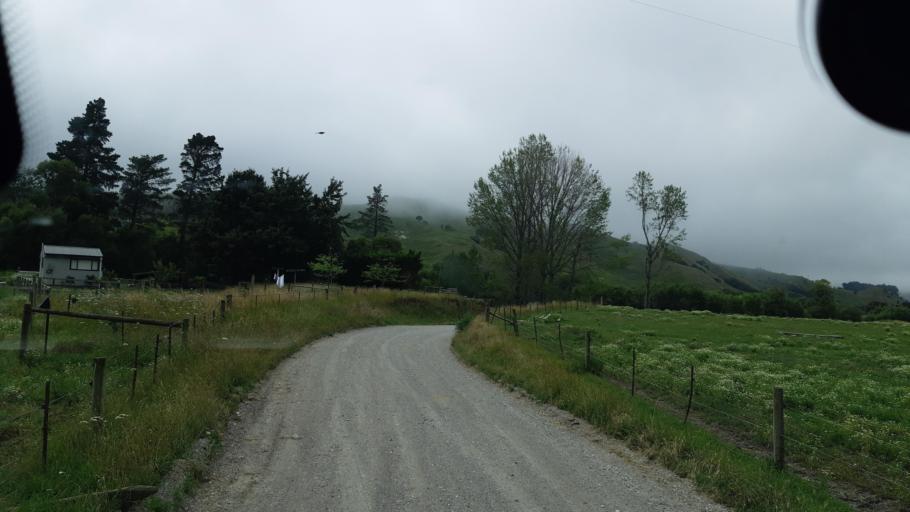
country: NZ
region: Marlborough
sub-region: Marlborough District
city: Blenheim
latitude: -41.9757
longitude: 173.9981
